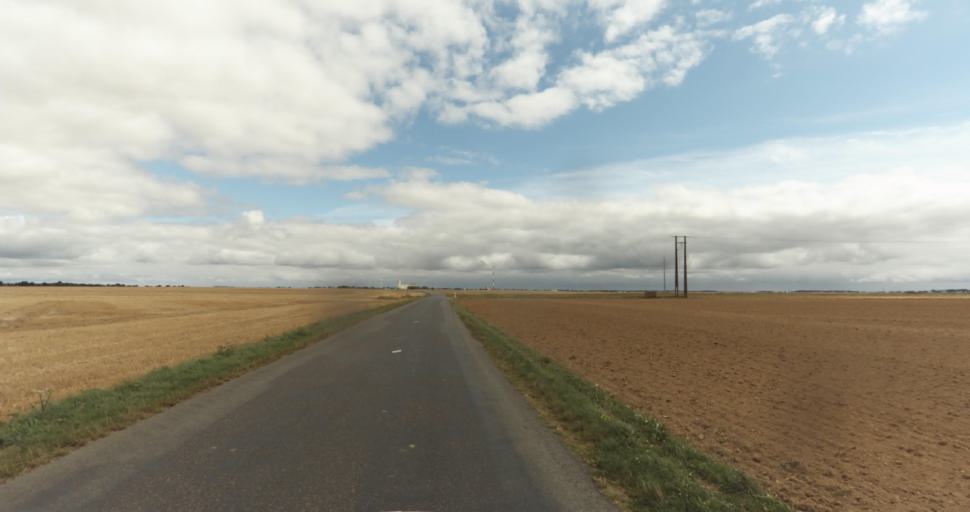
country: FR
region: Haute-Normandie
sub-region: Departement de l'Eure
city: Marcilly-sur-Eure
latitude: 48.9111
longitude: 1.2390
